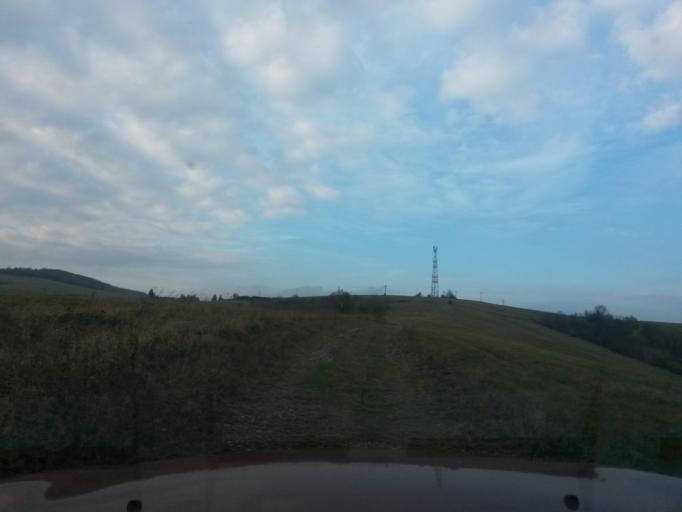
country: SK
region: Kosicky
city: Kosice
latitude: 48.7638
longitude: 21.2109
